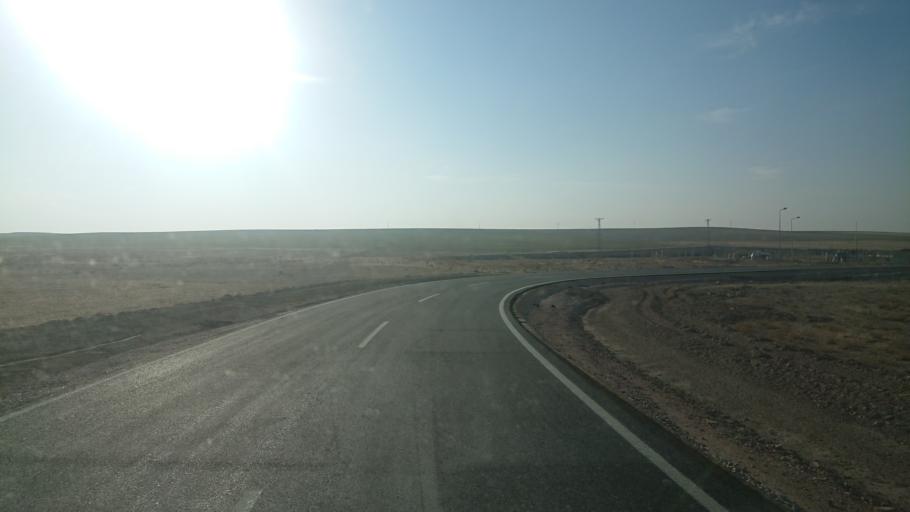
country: TR
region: Aksaray
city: Sultanhani
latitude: 38.0888
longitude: 33.6099
